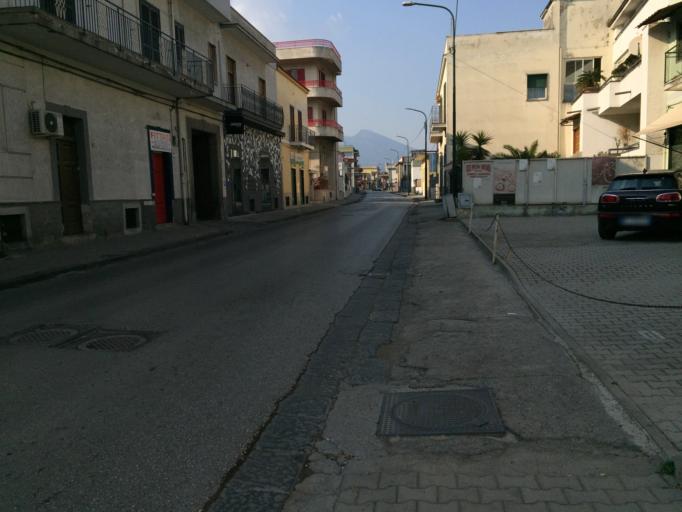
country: IT
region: Campania
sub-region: Provincia di Napoli
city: Pompei
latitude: 40.7538
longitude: 14.4989
